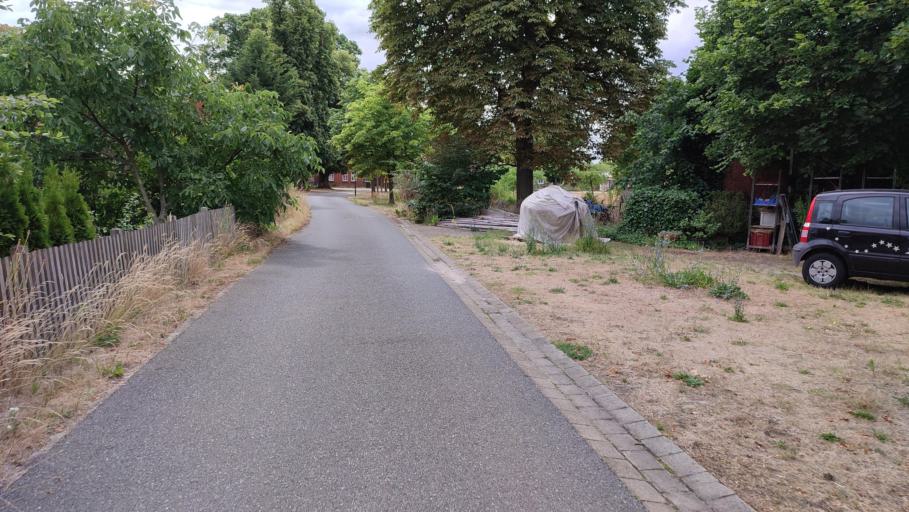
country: DE
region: Lower Saxony
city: Hitzacker
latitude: 53.1842
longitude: 11.1091
